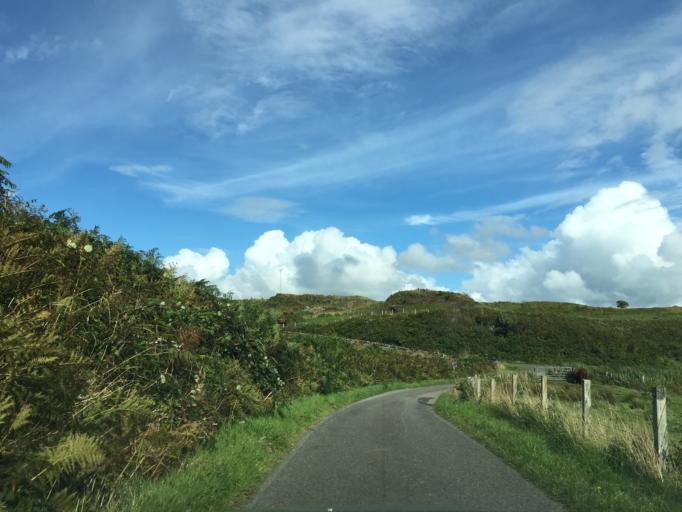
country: GB
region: Scotland
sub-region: Argyll and Bute
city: Isle Of Mull
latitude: 56.2490
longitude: -5.6466
